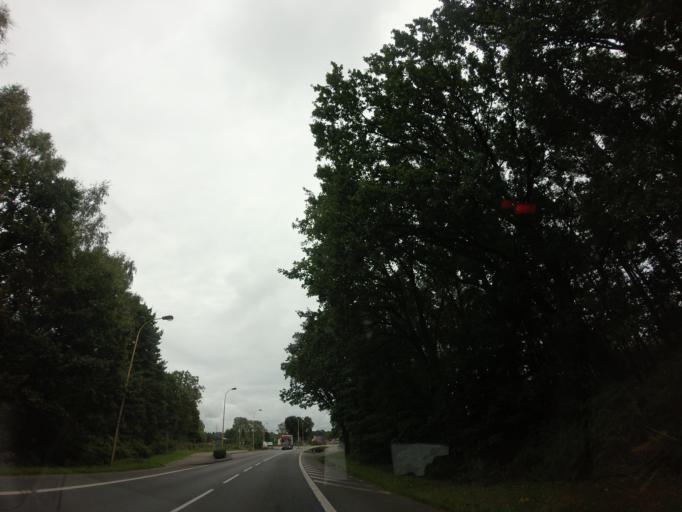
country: PL
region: West Pomeranian Voivodeship
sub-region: Powiat kamienski
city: Miedzyzdroje
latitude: 53.8961
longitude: 14.3544
